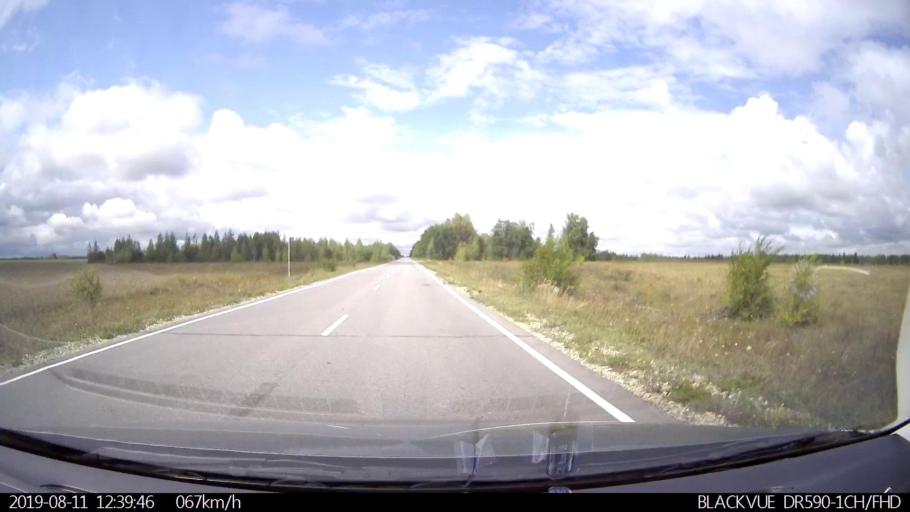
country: RU
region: Ulyanovsk
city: Ignatovka
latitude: 53.8350
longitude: 47.7906
